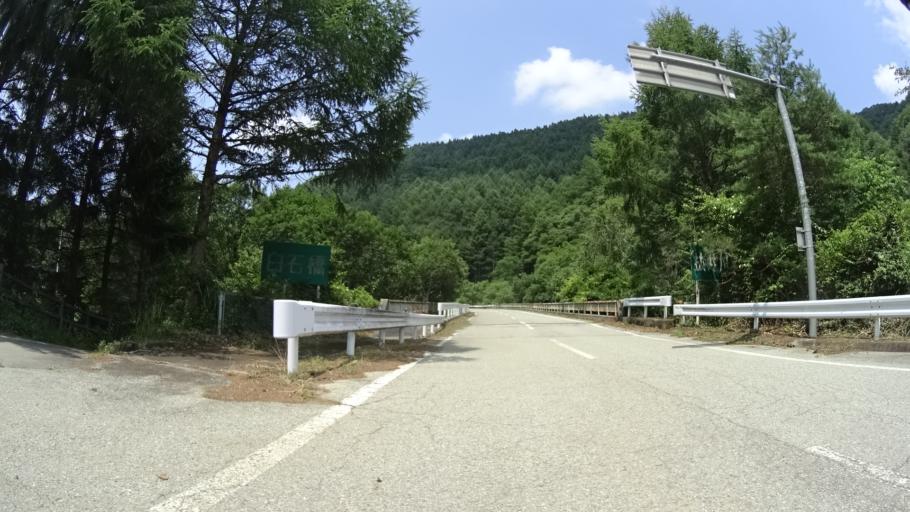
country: JP
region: Nagano
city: Saku
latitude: 36.1230
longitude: 138.6059
